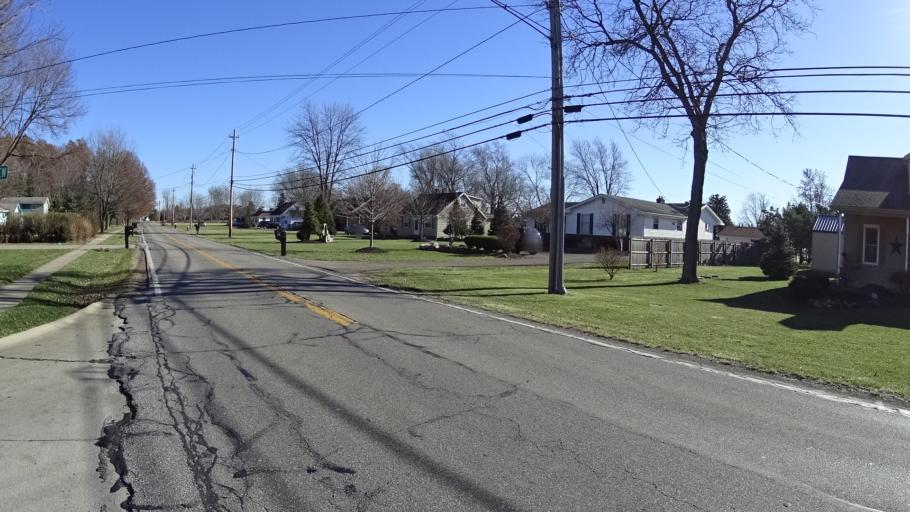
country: US
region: Ohio
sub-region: Lorain County
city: Avon
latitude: 41.4420
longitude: -82.0234
